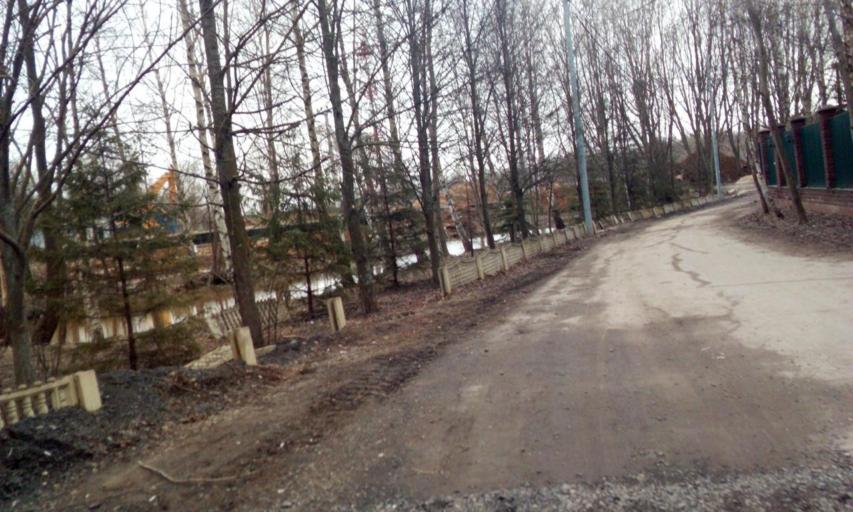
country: RU
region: Moskovskaya
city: Kommunarka
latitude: 55.5234
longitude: 37.5038
